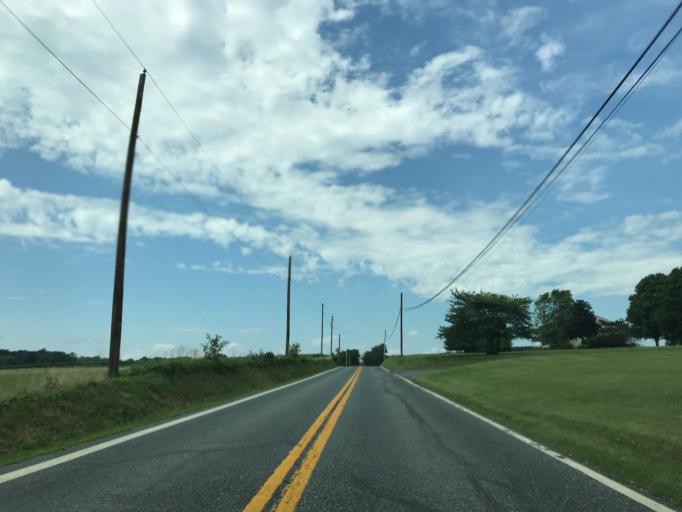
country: US
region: Pennsylvania
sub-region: York County
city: Susquehanna Trails
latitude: 39.6812
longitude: -76.4094
